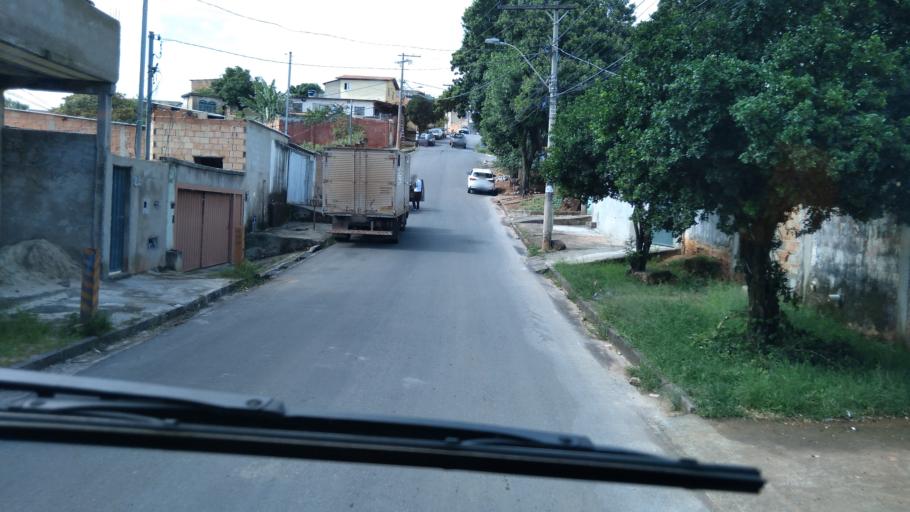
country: BR
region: Minas Gerais
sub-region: Santa Luzia
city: Santa Luzia
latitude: -19.8320
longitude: -43.8967
